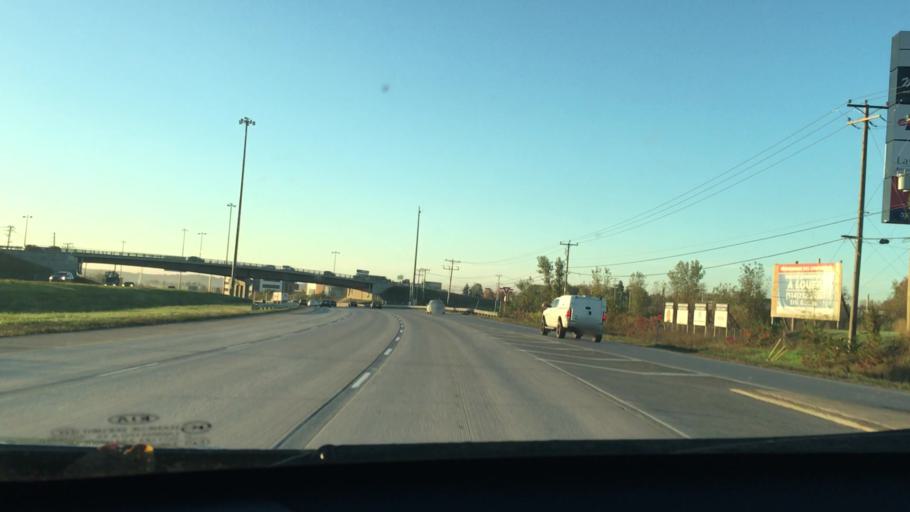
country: CA
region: Quebec
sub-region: Laurentides
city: Saint-Jerome
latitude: 45.7595
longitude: -74.0209
